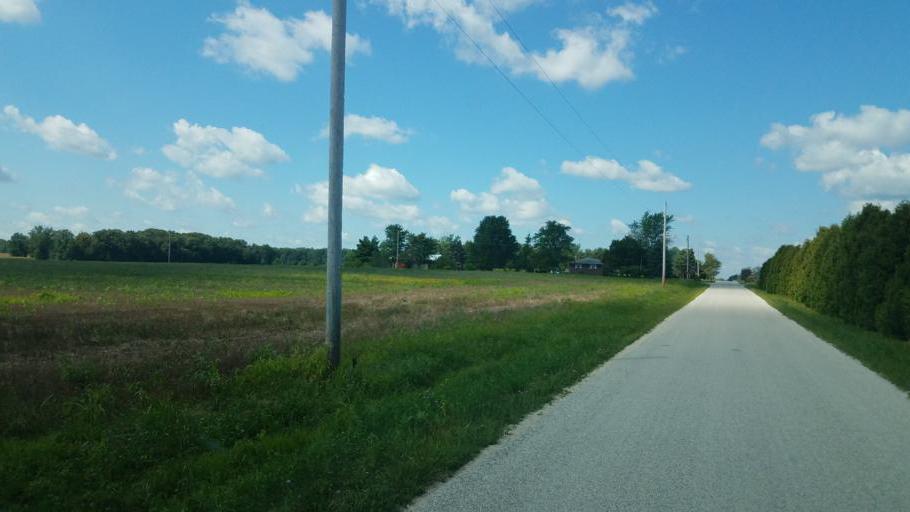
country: US
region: Ohio
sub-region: Wyandot County
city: Carey
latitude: 41.0143
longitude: -83.3225
